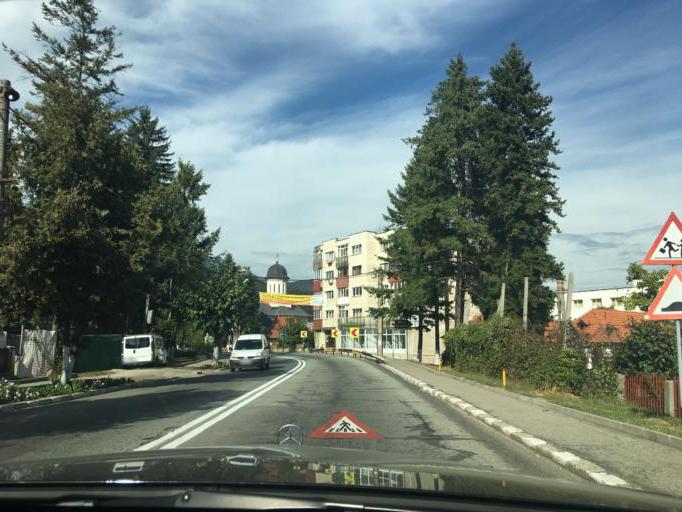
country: RO
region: Valcea
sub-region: Oras Calimanesti
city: Calimanesti
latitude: 45.2393
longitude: 24.3414
